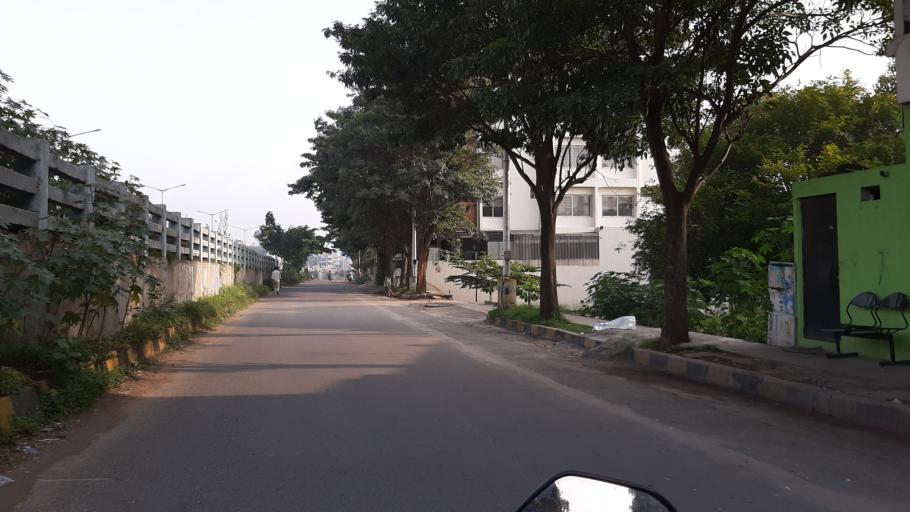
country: IN
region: Karnataka
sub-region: Bangalore Urban
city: Bangalore
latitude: 12.9719
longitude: 77.5130
